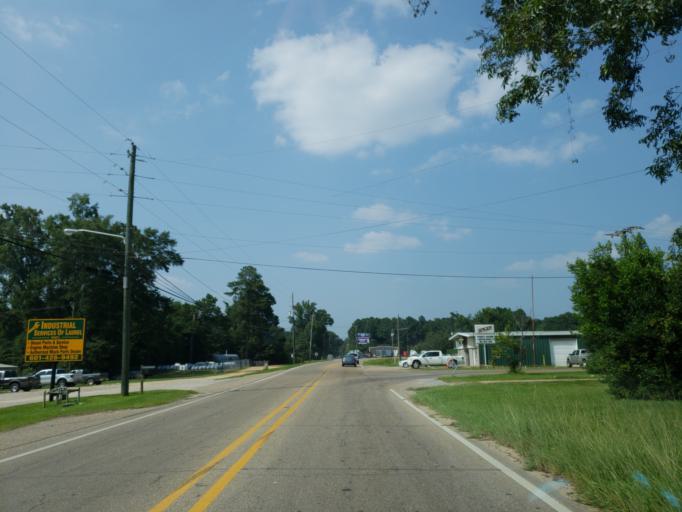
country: US
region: Mississippi
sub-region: Jones County
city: Ellisville
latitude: 31.6363
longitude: -89.1809
